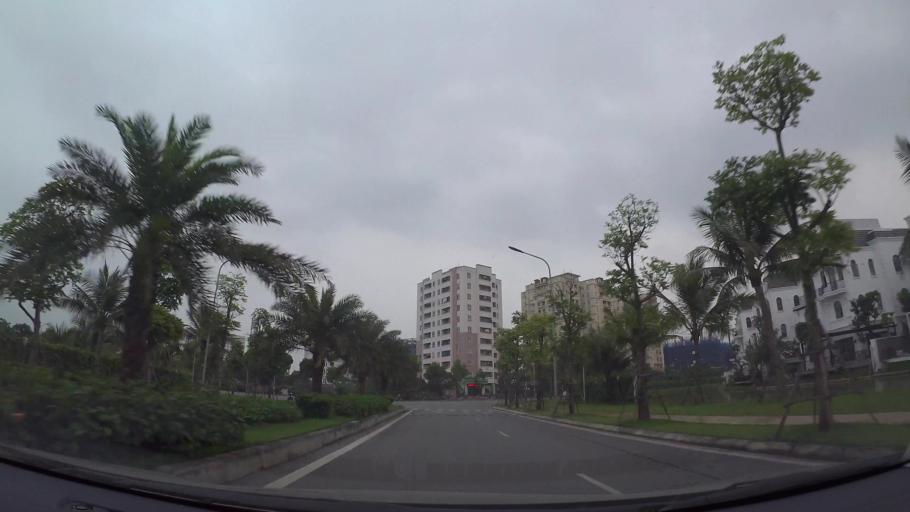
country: VN
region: Ha Noi
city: Trau Quy
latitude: 21.0412
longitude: 105.9084
